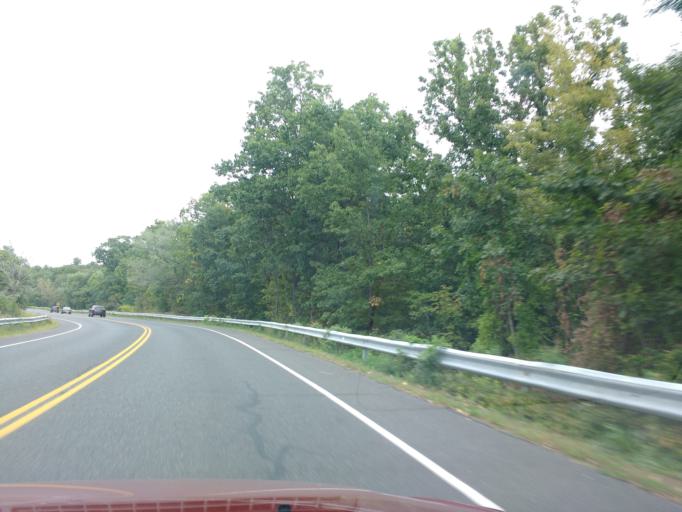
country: US
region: New York
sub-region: Ulster County
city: Lincoln Park
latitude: 41.9646
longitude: -73.9818
